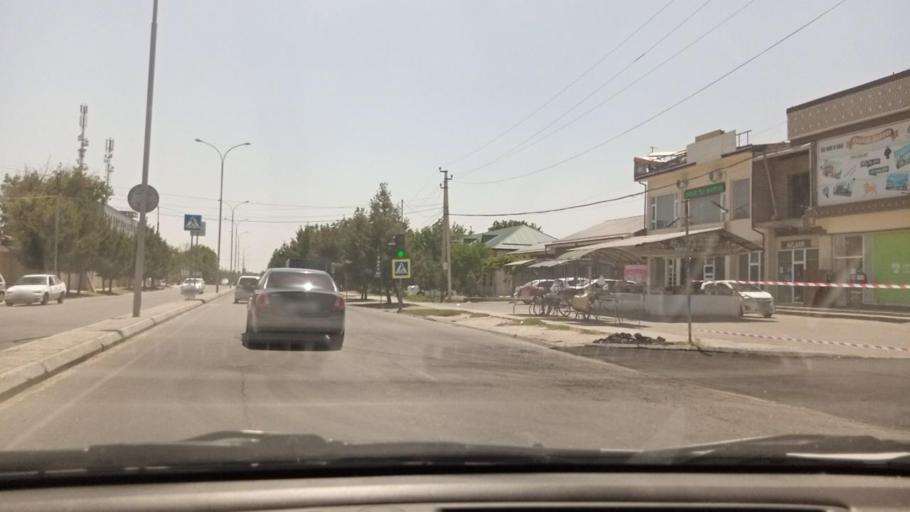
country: UZ
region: Toshkent
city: Urtaowul
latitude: 41.2256
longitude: 69.1791
